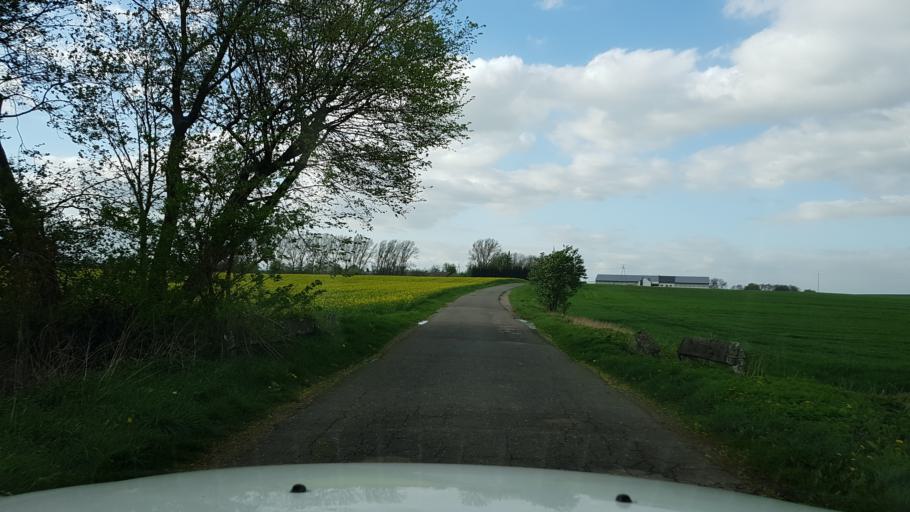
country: PL
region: West Pomeranian Voivodeship
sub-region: Powiat pyrzycki
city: Przelewice
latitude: 53.0699
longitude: 15.1018
